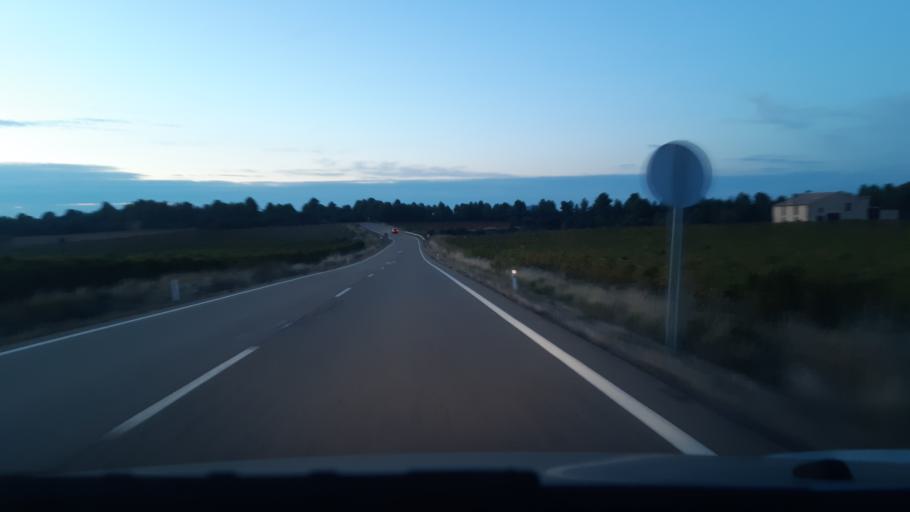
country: ES
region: Aragon
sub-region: Provincia de Teruel
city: Calaceite
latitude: 40.9594
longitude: 0.2146
